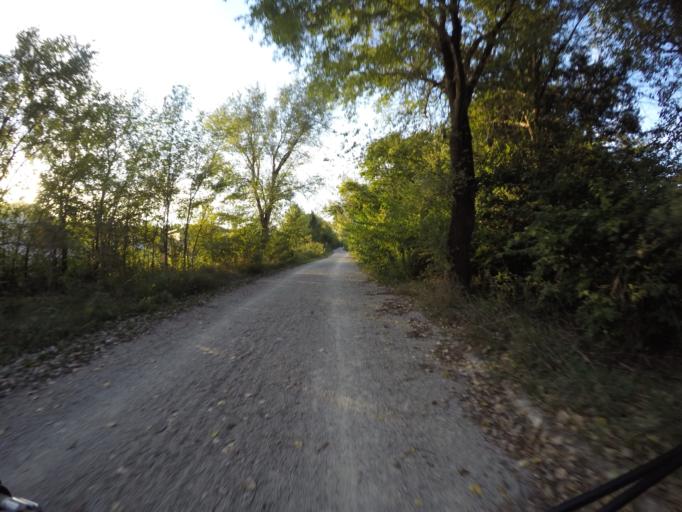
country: US
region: Kansas
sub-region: Riley County
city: Manhattan
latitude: 39.1793
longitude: -96.6048
